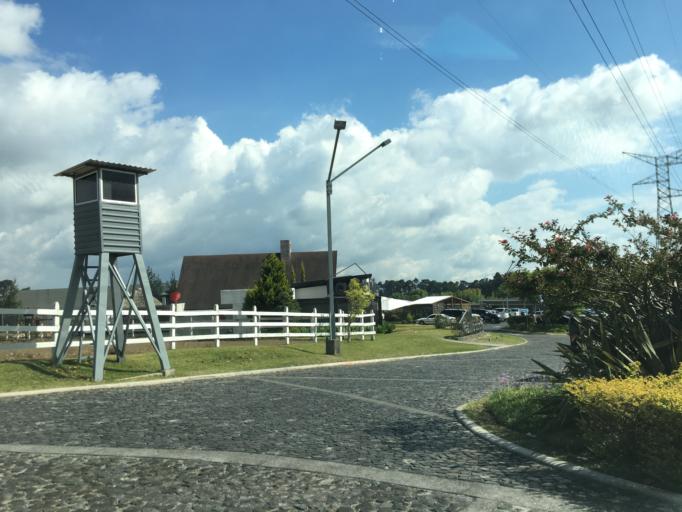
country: GT
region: Guatemala
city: Fraijanes
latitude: 14.4964
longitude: -90.4809
